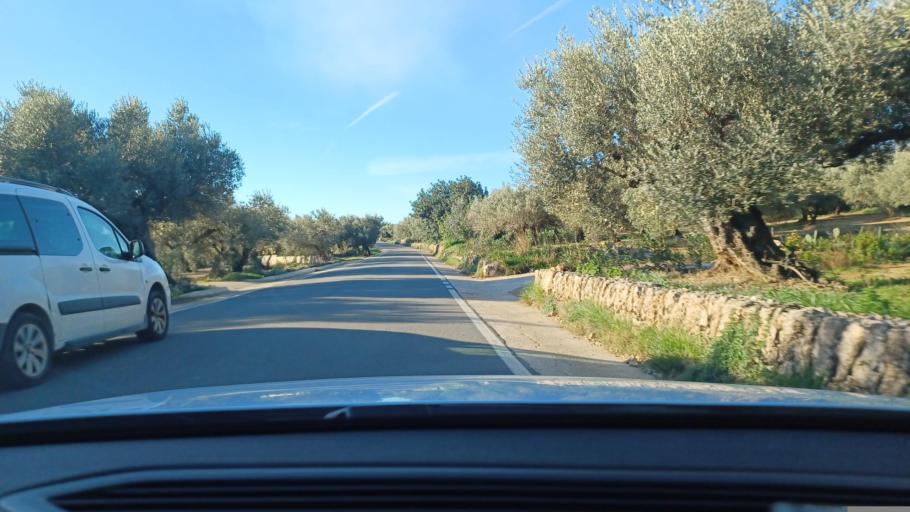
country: ES
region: Catalonia
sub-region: Provincia de Tarragona
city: Mas de Barberans
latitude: 40.7224
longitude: 0.3664
